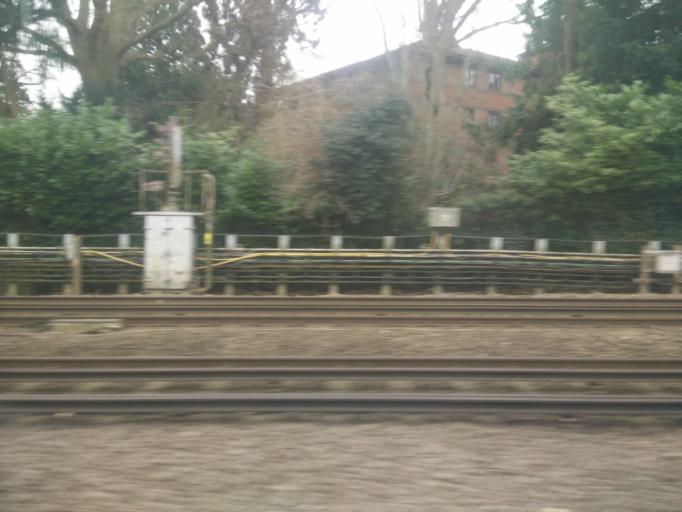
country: GB
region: England
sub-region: Greater London
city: Pinner
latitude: 51.5944
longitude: -0.3850
